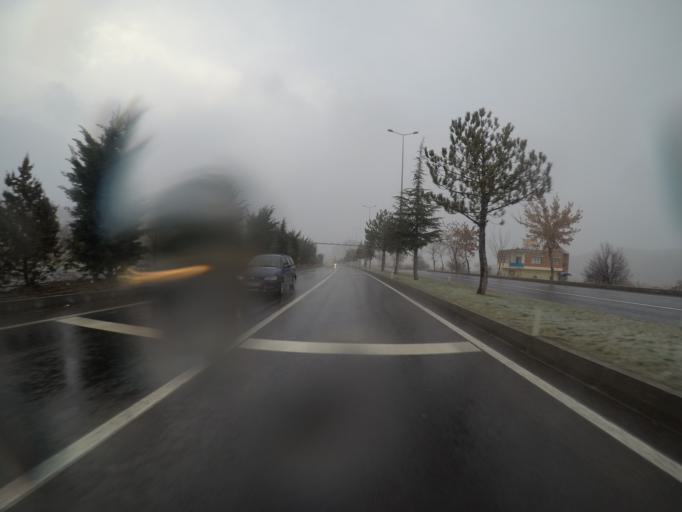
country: TR
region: Nevsehir
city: Nevsehir
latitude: 38.6320
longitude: 34.7497
